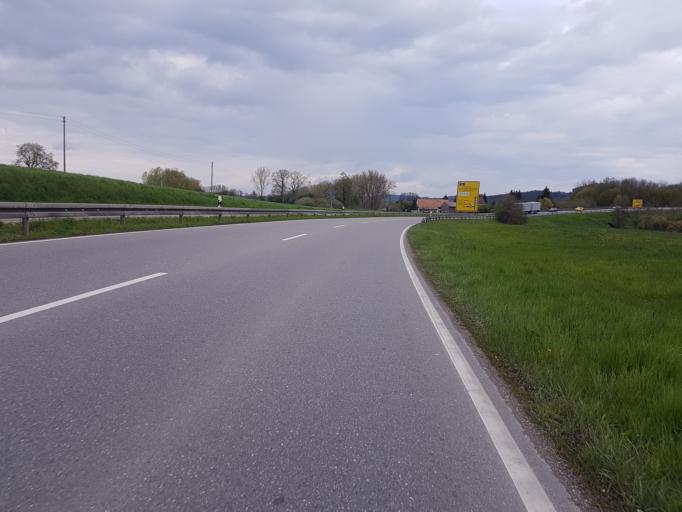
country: DE
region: Baden-Wuerttemberg
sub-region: Freiburg Region
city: Donaueschingen
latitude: 47.9692
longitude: 8.5068
